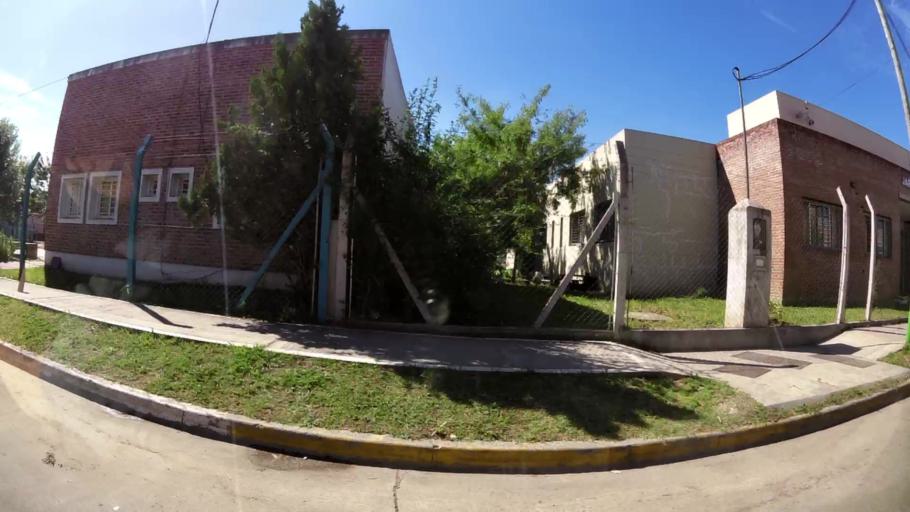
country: AR
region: Buenos Aires
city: Hurlingham
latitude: -34.6204
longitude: -58.6499
